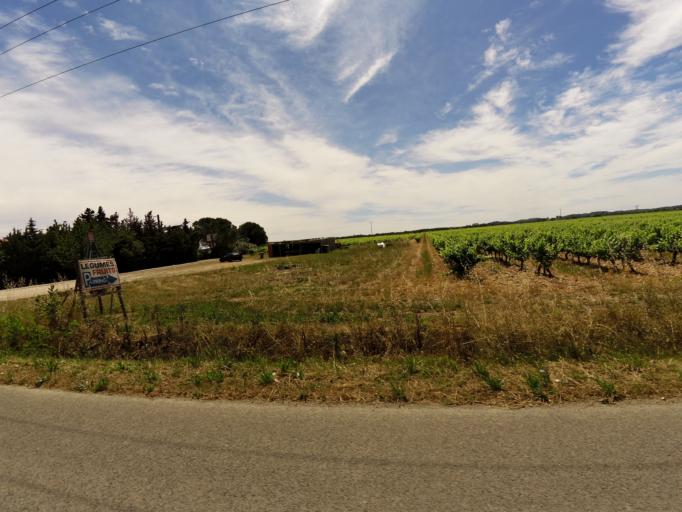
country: FR
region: Languedoc-Roussillon
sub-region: Departement du Gard
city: Aubord
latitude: 43.7667
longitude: 4.3220
